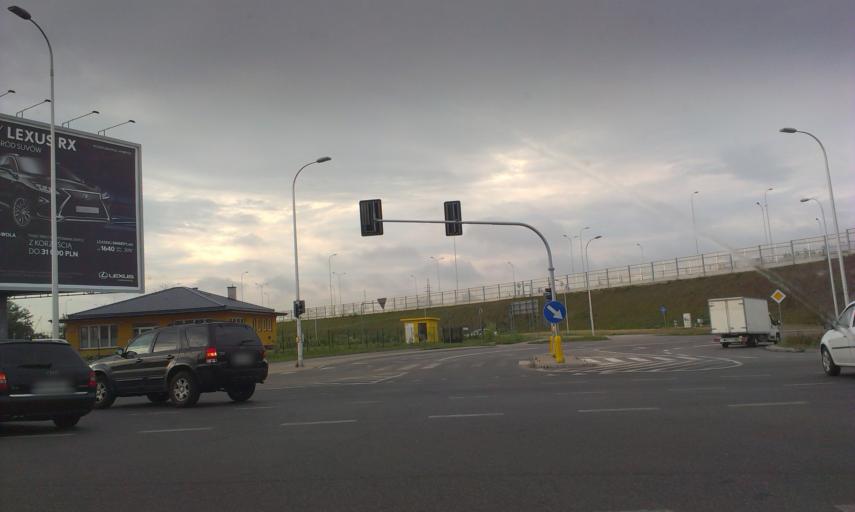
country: PL
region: Masovian Voivodeship
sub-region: Powiat pruszkowski
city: Michalowice
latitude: 52.1811
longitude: 20.8861
